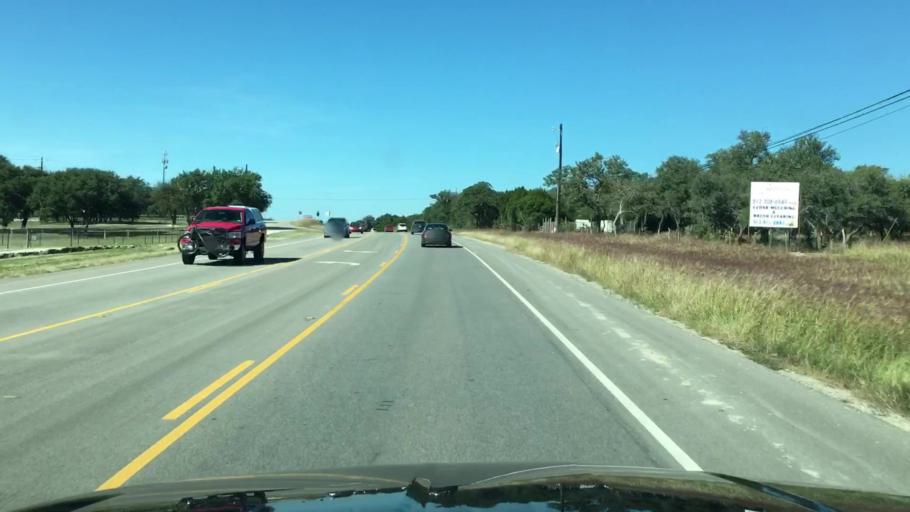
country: US
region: Texas
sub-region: Hays County
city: Dripping Springs
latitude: 30.1996
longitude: -98.1836
